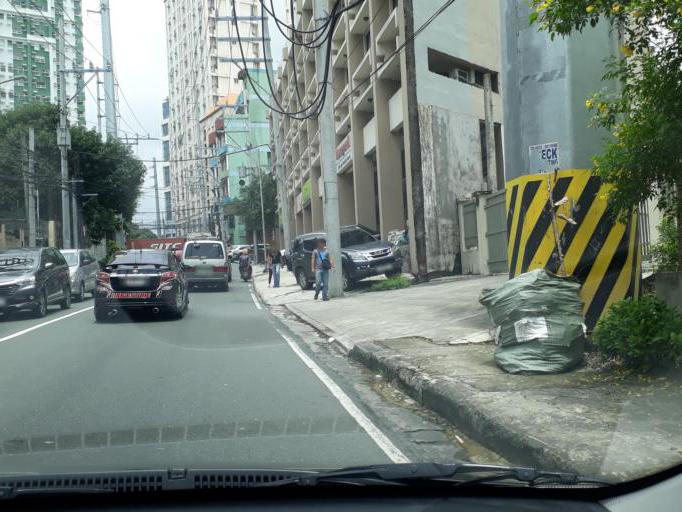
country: PH
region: Metro Manila
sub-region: San Juan
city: San Juan
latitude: 14.6114
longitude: 121.0347
